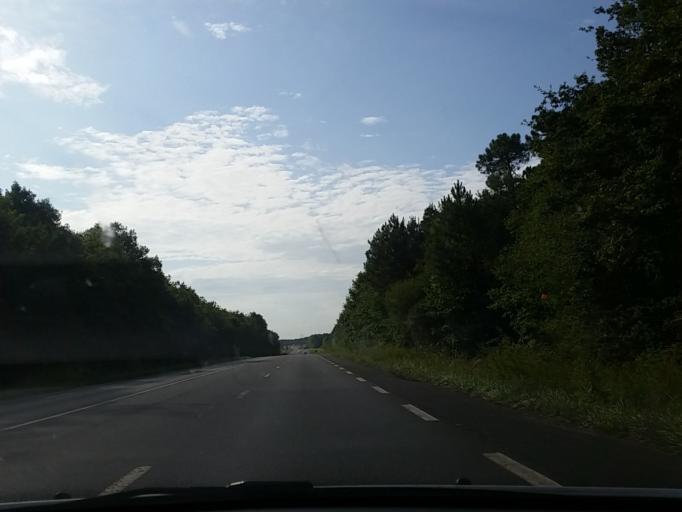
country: FR
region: Centre
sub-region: Departement du Loir-et-Cher
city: Soings-en-Sologne
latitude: 47.4525
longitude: 1.5320
